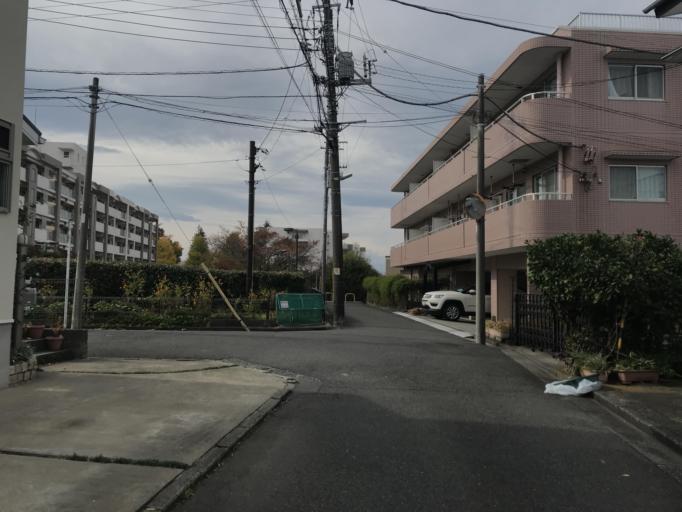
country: JP
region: Kanagawa
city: Yokohama
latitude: 35.4716
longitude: 139.6229
